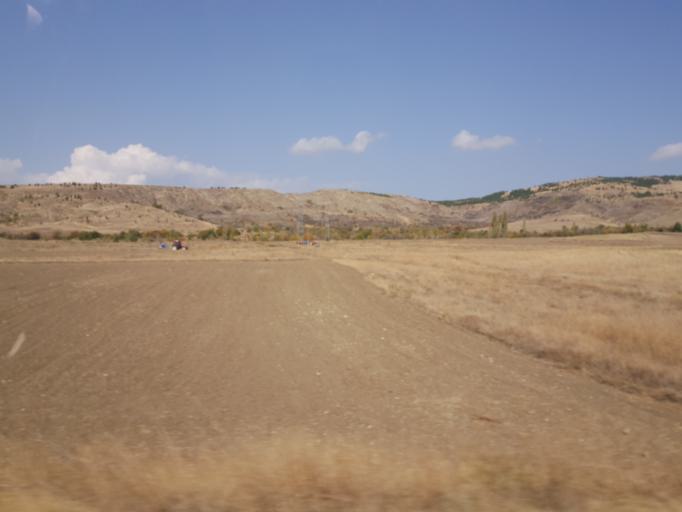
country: TR
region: Corum
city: Bogazkale
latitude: 40.1581
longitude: 34.6188
